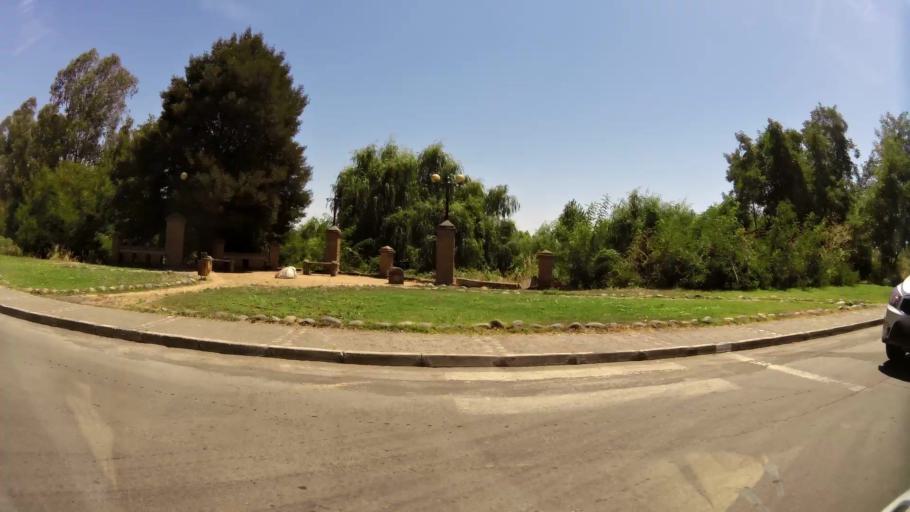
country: CL
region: Maule
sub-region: Provincia de Curico
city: Curico
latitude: -34.9910
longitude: -71.2105
